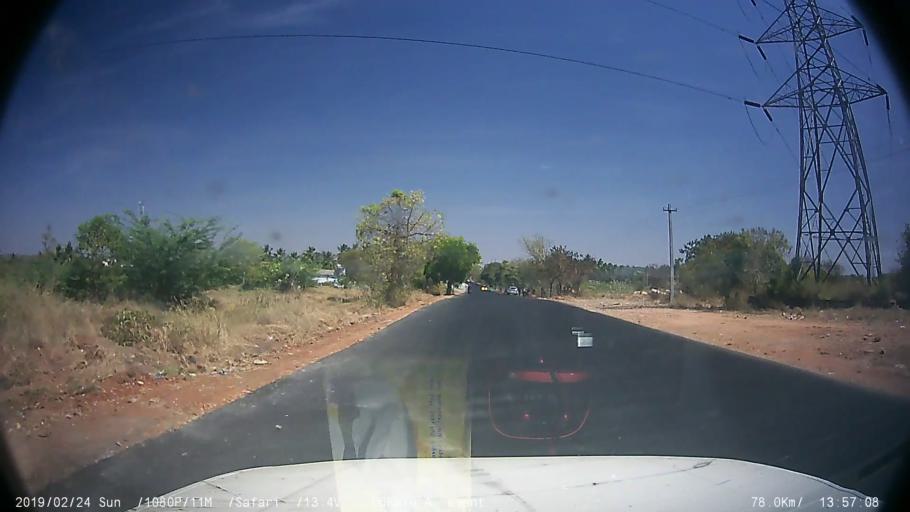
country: IN
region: Tamil Nadu
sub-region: Coimbatore
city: Sirumugai
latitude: 11.2653
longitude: 77.0222
